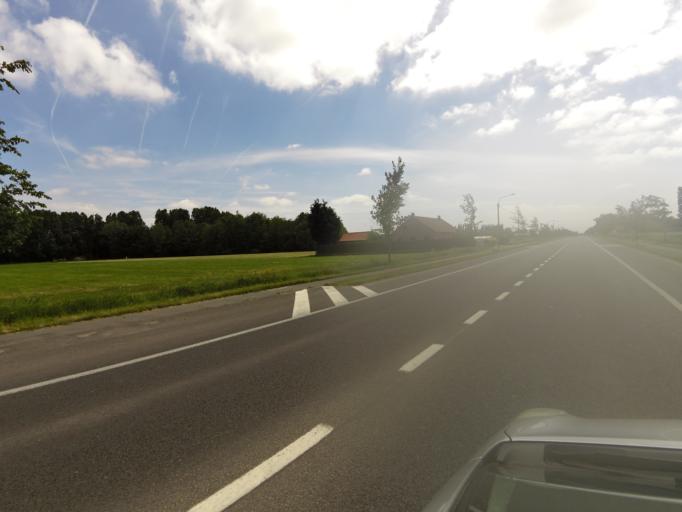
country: BE
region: Flanders
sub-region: Provincie West-Vlaanderen
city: Diksmuide
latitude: 51.0721
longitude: 2.8751
